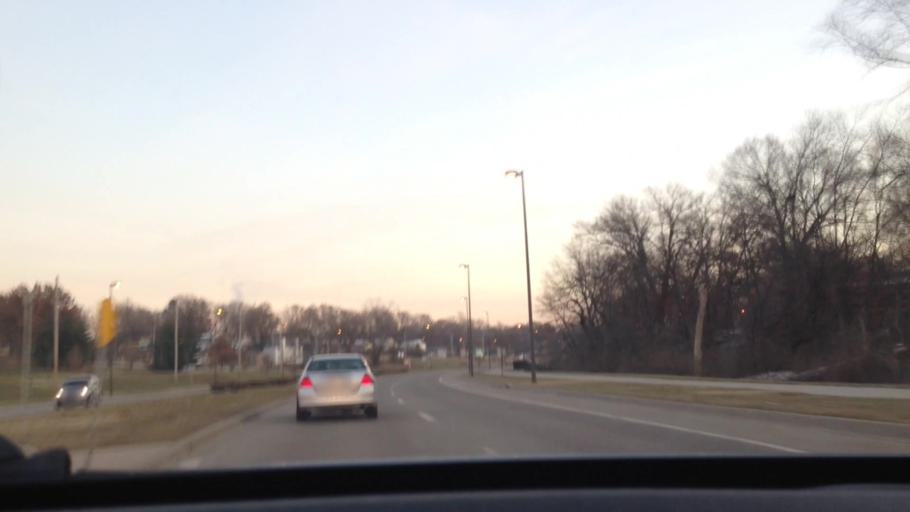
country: US
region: Missouri
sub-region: Clay County
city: Gladstone
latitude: 39.1723
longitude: -94.5346
